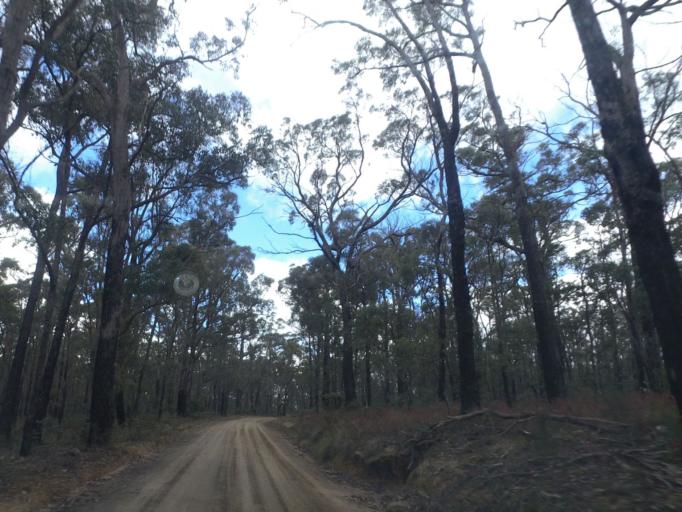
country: AU
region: Victoria
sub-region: Moorabool
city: Bacchus Marsh
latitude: -37.4860
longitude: 144.4732
